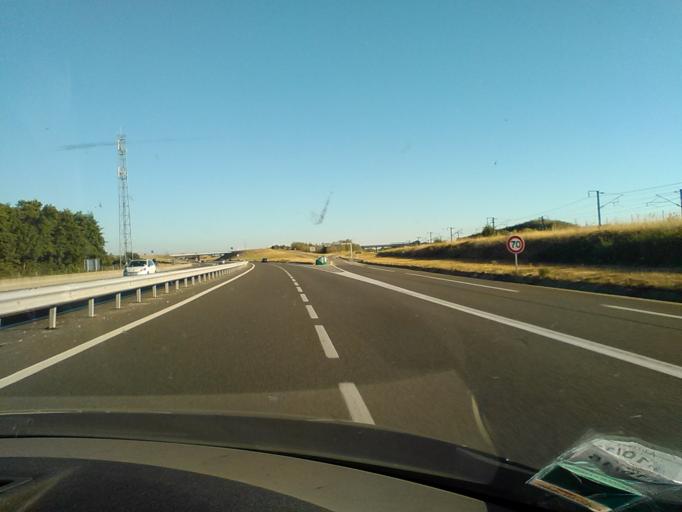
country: FR
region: Rhone-Alpes
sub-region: Departement du Rhone
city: Pusignan
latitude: 45.7707
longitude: 5.0832
